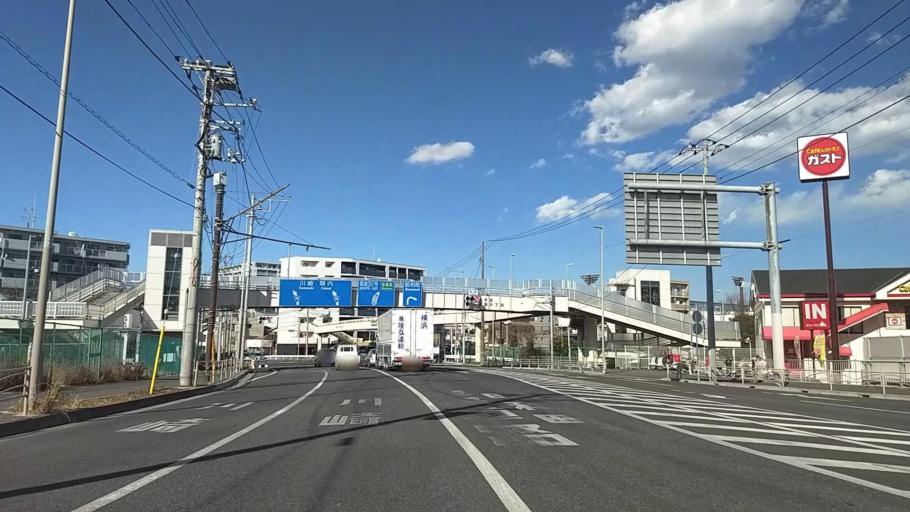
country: JP
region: Kanagawa
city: Yokohama
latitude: 35.3806
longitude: 139.6223
